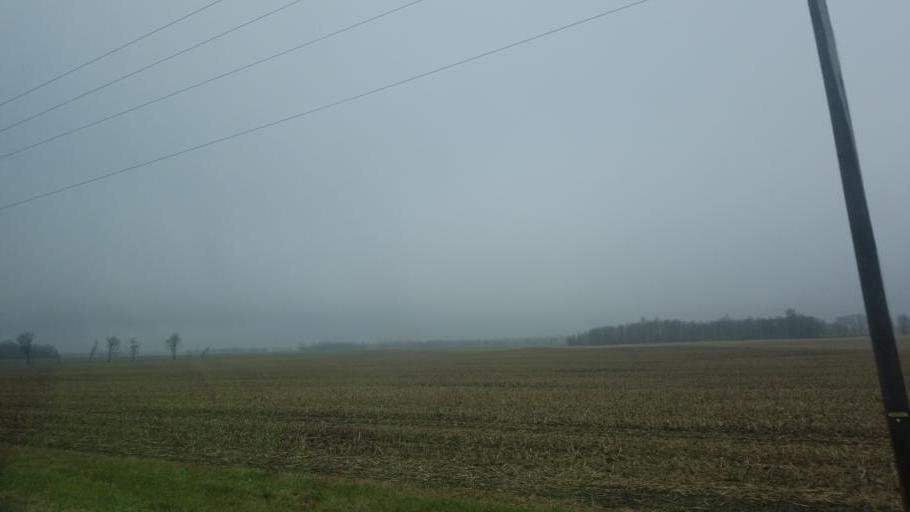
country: US
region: Ohio
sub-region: Champaign County
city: North Lewisburg
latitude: 40.2349
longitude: -83.5637
